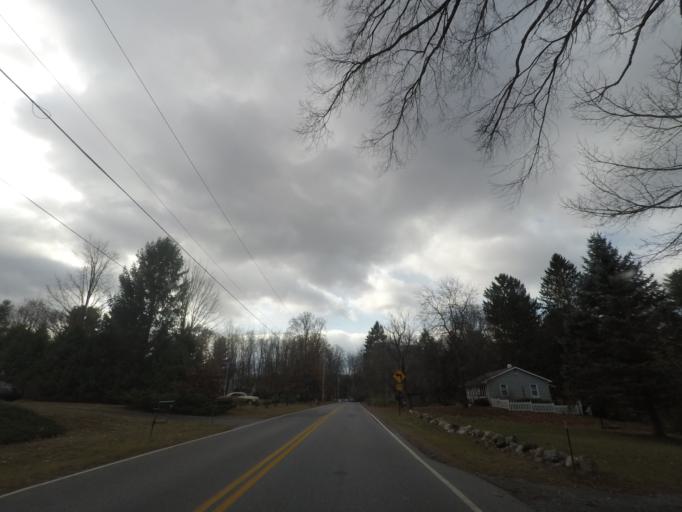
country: US
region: New York
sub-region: Saratoga County
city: Ballston Spa
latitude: 43.0108
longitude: -73.8069
